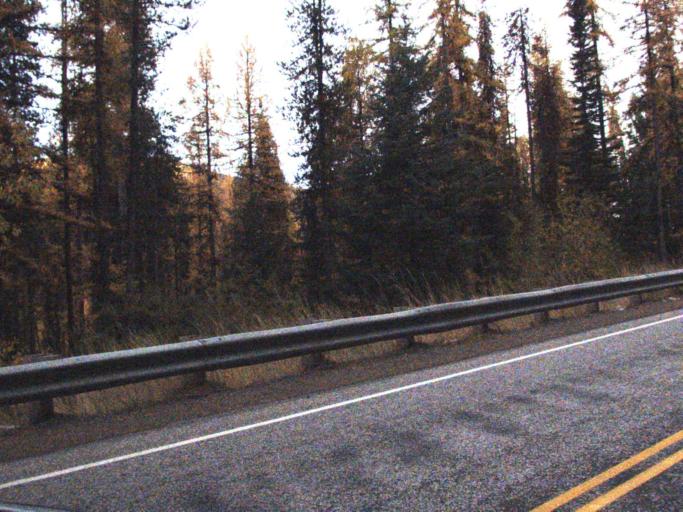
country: US
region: Washington
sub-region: Ferry County
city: Republic
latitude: 48.6182
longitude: -118.4436
